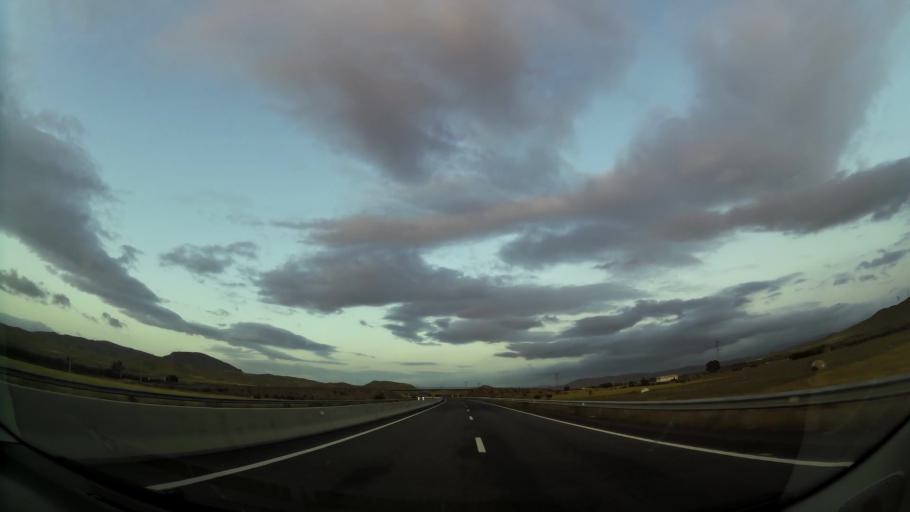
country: MA
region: Oriental
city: El Aioun
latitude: 34.5938
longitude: -2.6982
